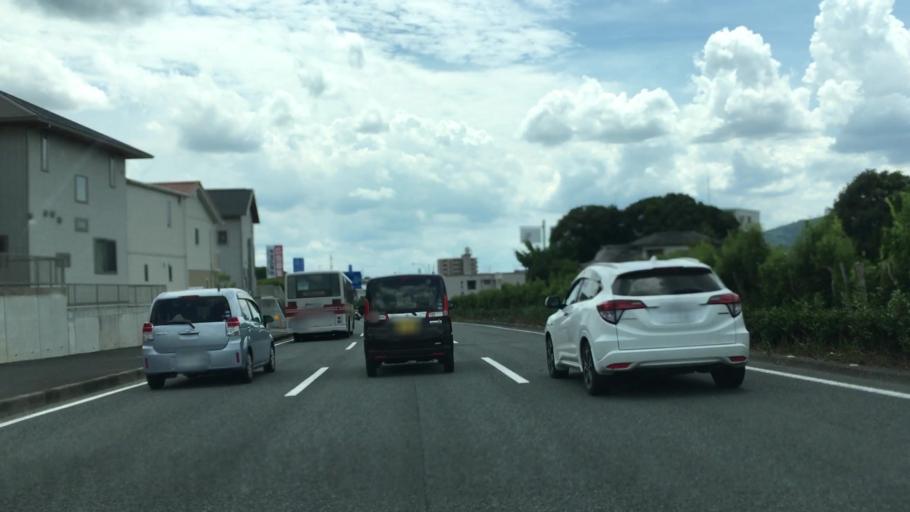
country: JP
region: Fukuoka
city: Chikushino-shi
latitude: 33.4890
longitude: 130.5356
